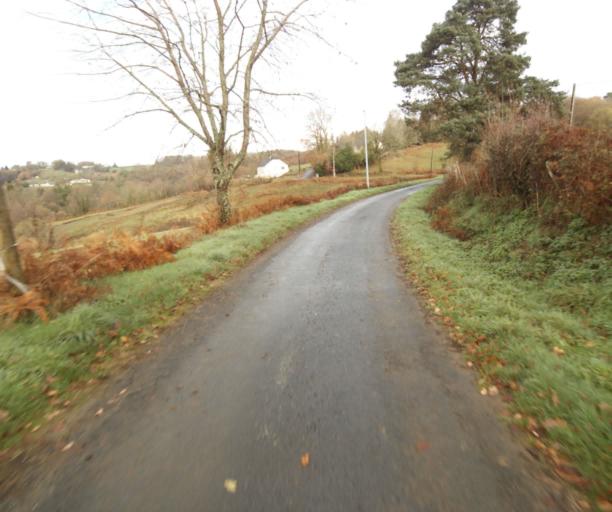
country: FR
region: Limousin
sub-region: Departement de la Correze
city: Saint-Mexant
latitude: 45.2504
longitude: 1.6469
